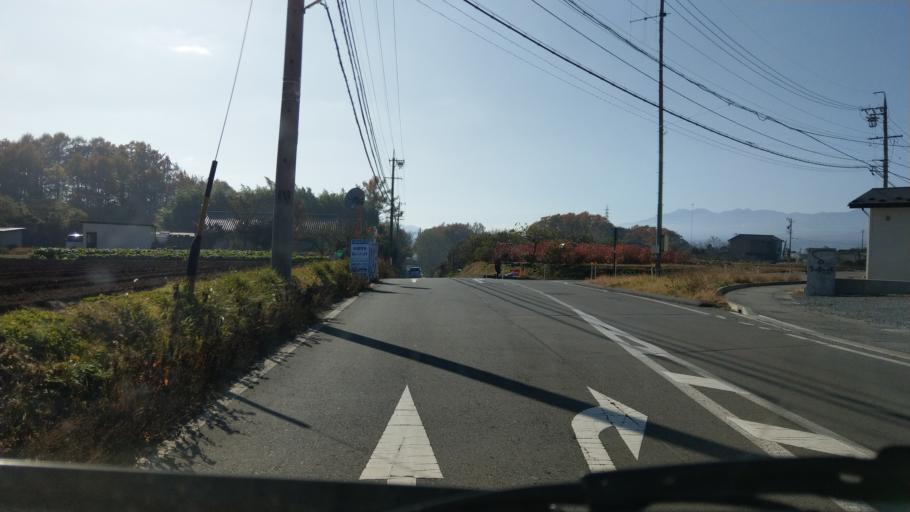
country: JP
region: Nagano
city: Komoro
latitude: 36.2977
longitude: 138.4855
